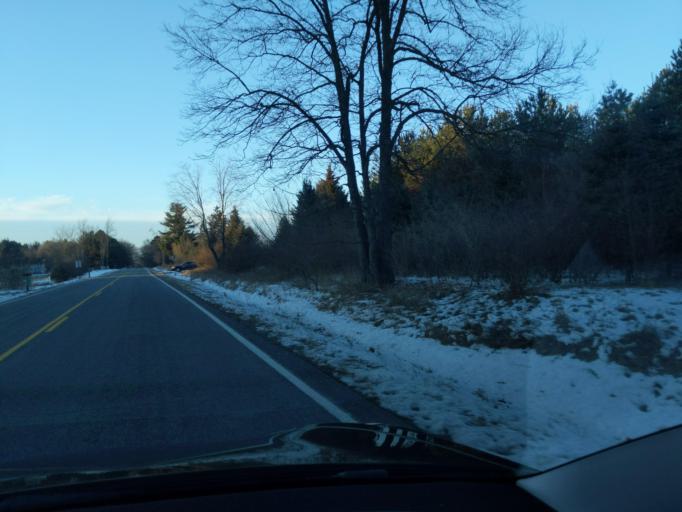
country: US
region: Michigan
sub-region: Ingham County
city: Stockbridge
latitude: 42.5204
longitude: -84.2718
